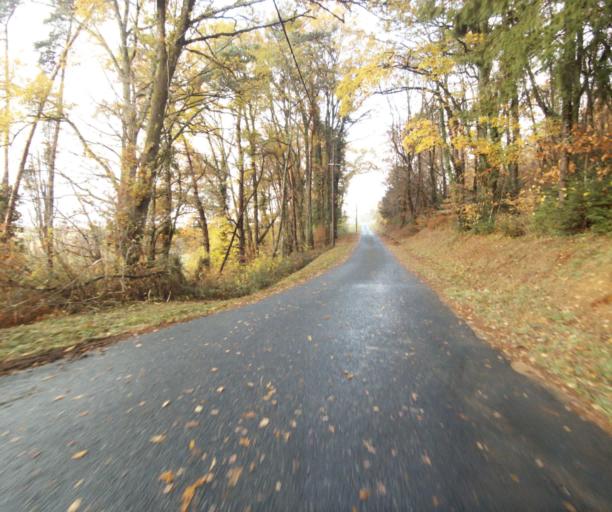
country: FR
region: Limousin
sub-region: Departement de la Correze
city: Cornil
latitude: 45.2171
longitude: 1.6629
